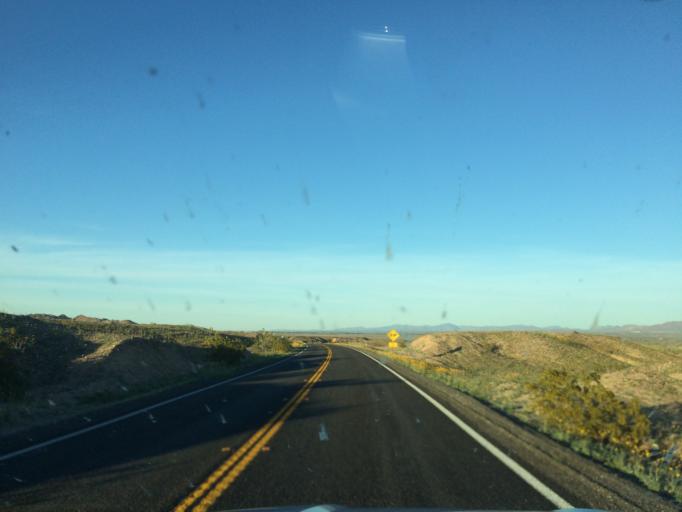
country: US
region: California
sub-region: Riverside County
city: Mesa Verde
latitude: 33.2920
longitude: -114.7537
